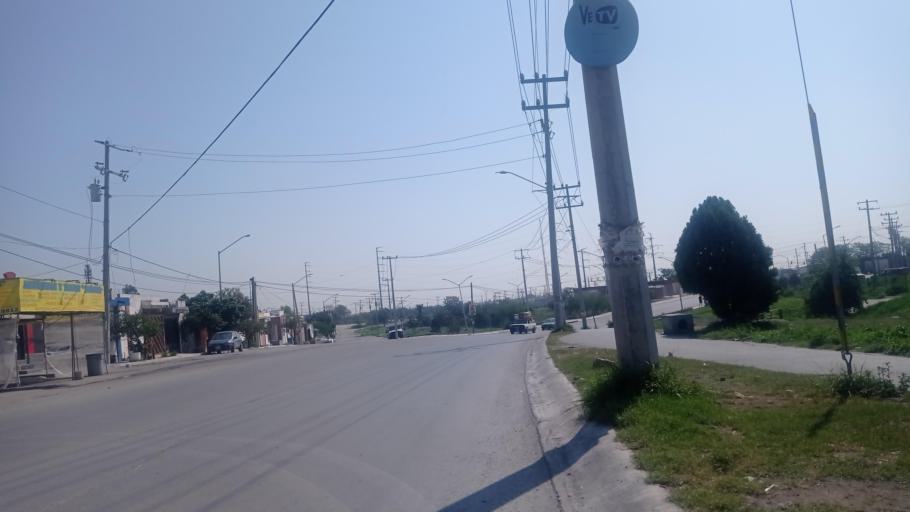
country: MX
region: Nuevo Leon
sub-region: Juarez
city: Monte Kristal
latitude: 25.6103
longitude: -100.1596
